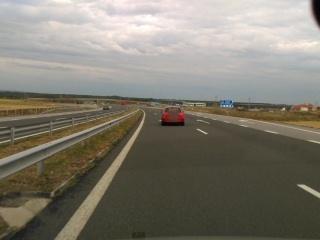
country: BG
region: Yambol
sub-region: Obshtina Yambol
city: Yambol
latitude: 42.5393
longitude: 26.4780
